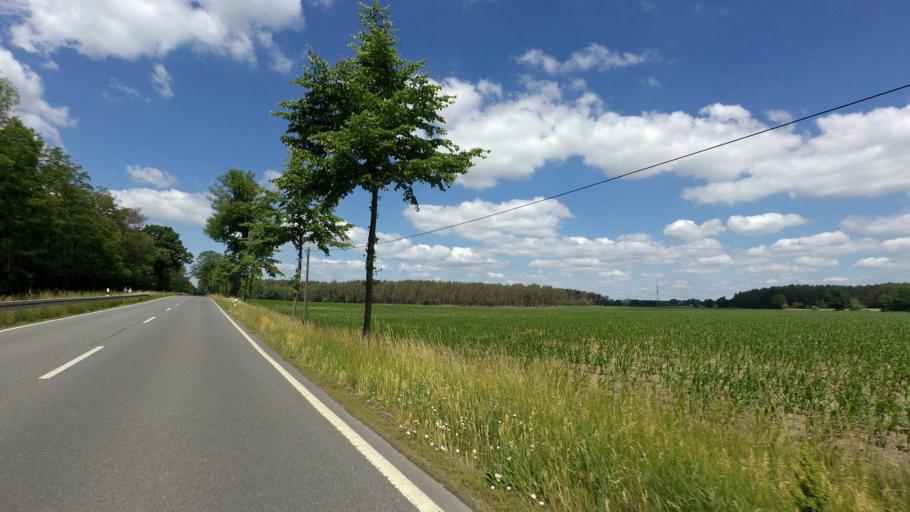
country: DE
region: Brandenburg
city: Finsterwalde
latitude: 51.6502
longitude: 13.6828
